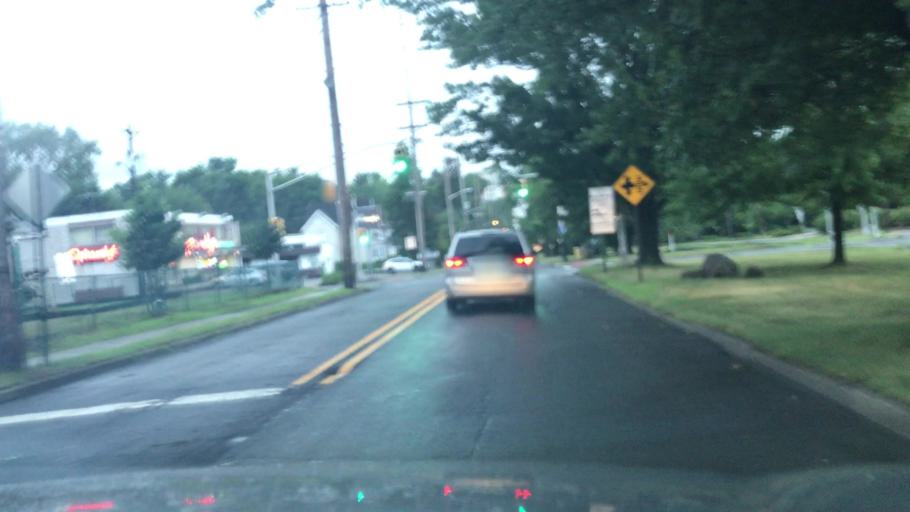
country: US
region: New Jersey
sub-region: Bergen County
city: Tenafly
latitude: 40.9106
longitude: -73.9679
